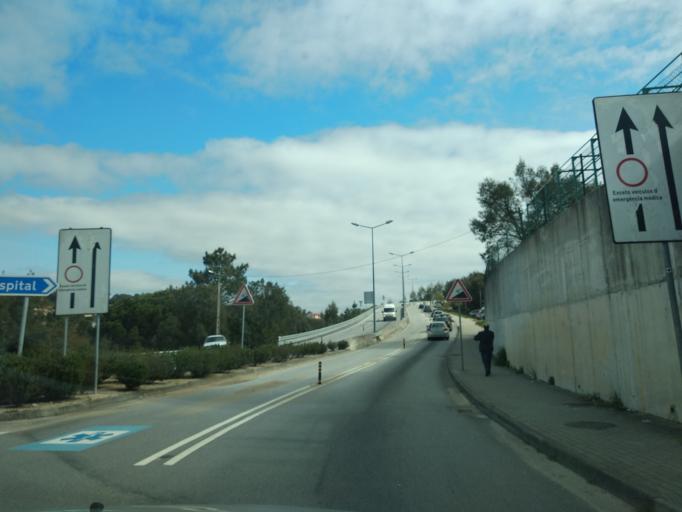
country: PT
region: Braga
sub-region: Braga
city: Adaufe
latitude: 41.5665
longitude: -8.4036
